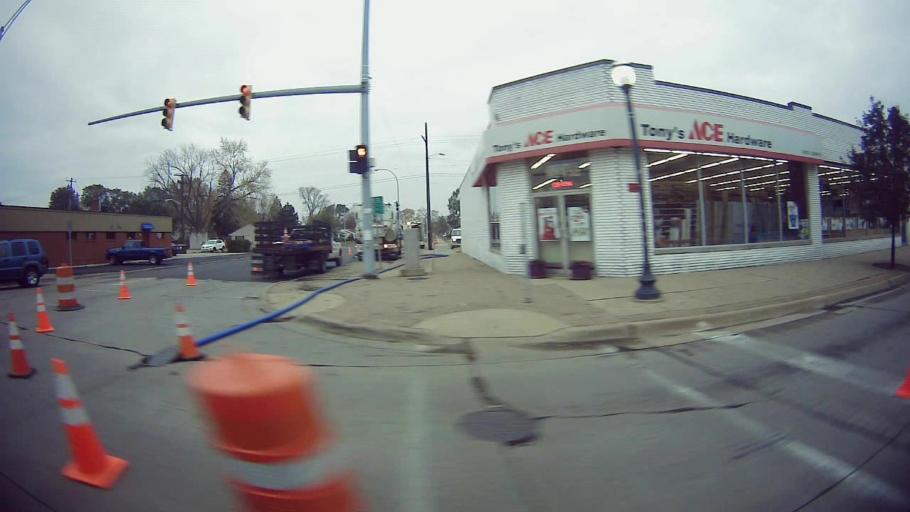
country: US
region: Michigan
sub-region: Oakland County
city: Hazel Park
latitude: 42.4694
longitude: -83.1044
